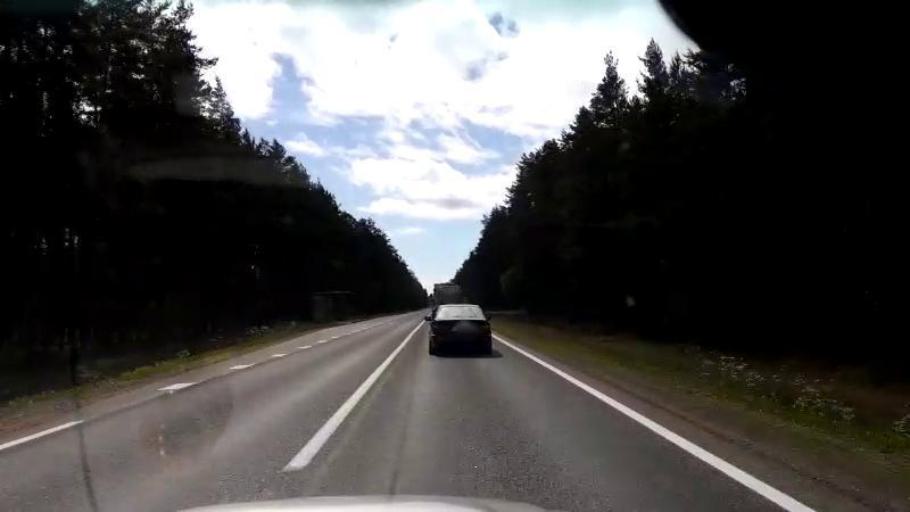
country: LV
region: Salacgrivas
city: Salacgriva
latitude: 57.5368
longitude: 24.4315
